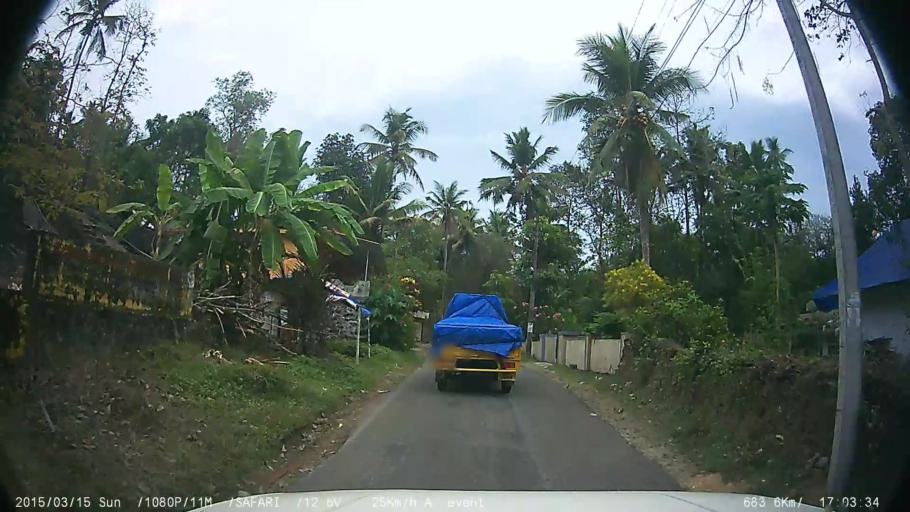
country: IN
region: Kerala
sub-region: Ernakulam
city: Muvattupuzha
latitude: 9.8755
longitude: 76.6519
